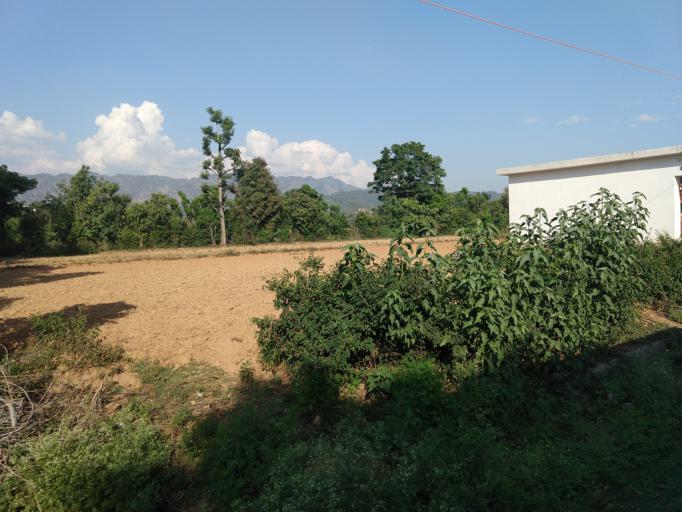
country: IN
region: Himachal Pradesh
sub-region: Chamba
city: Chowari
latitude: 32.3667
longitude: 75.9212
